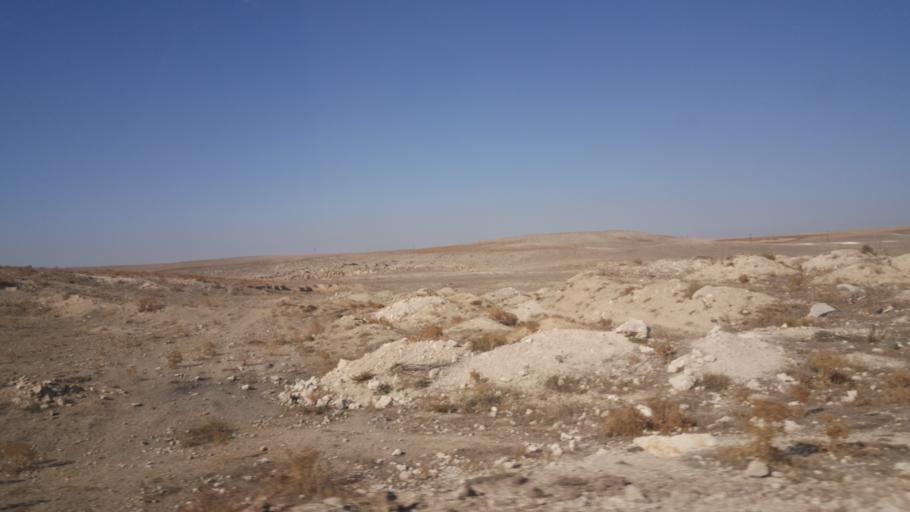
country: TR
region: Konya
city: Celtik
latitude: 39.0600
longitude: 31.8538
